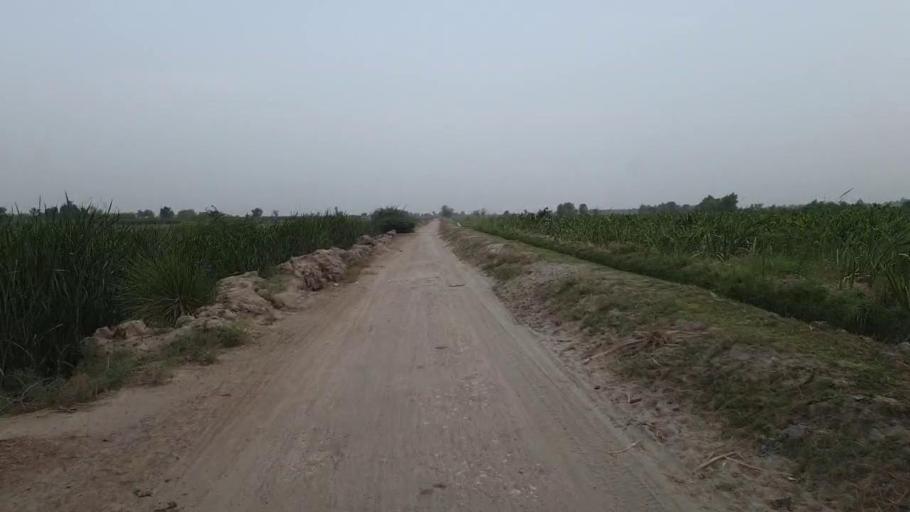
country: PK
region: Sindh
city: Daur
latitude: 26.4142
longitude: 68.2251
